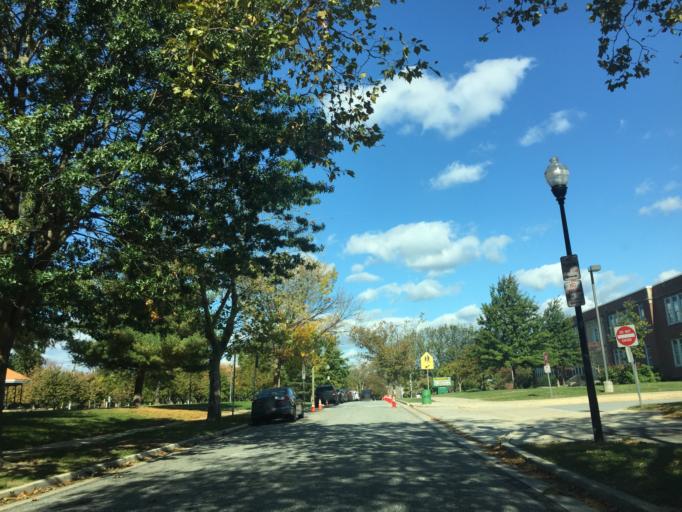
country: US
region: Maryland
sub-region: Baltimore County
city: Dundalk
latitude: 39.2577
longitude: -76.5197
